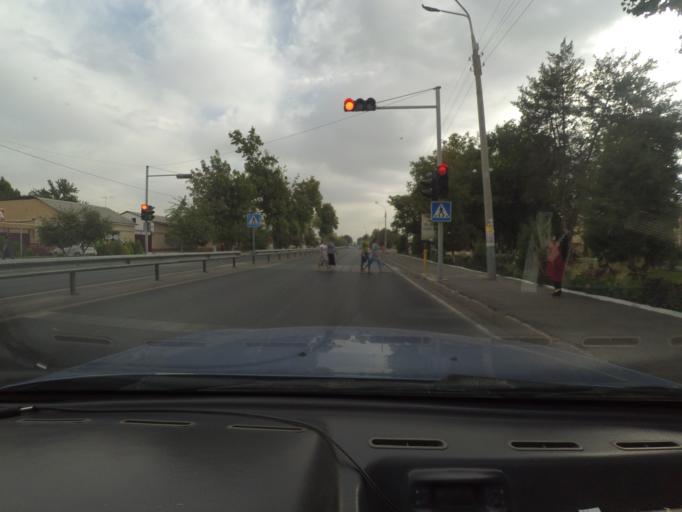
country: UZ
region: Toshkent
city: Qibray
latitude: 41.3727
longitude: 69.4276
